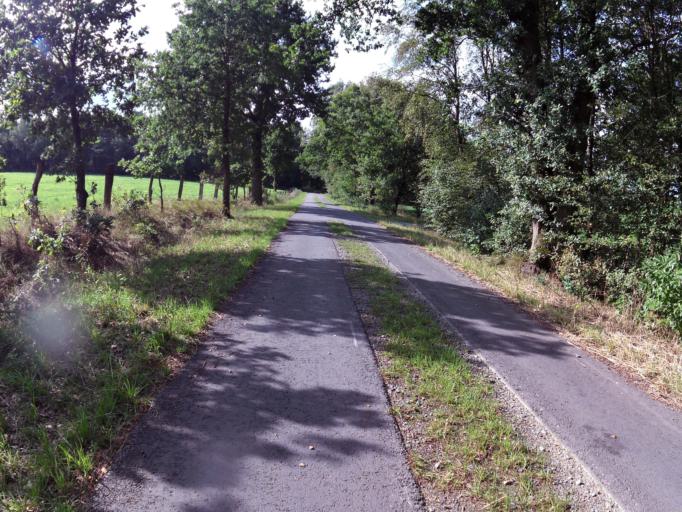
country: DE
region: Lower Saxony
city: Bremervorde
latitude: 53.4497
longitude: 9.1259
